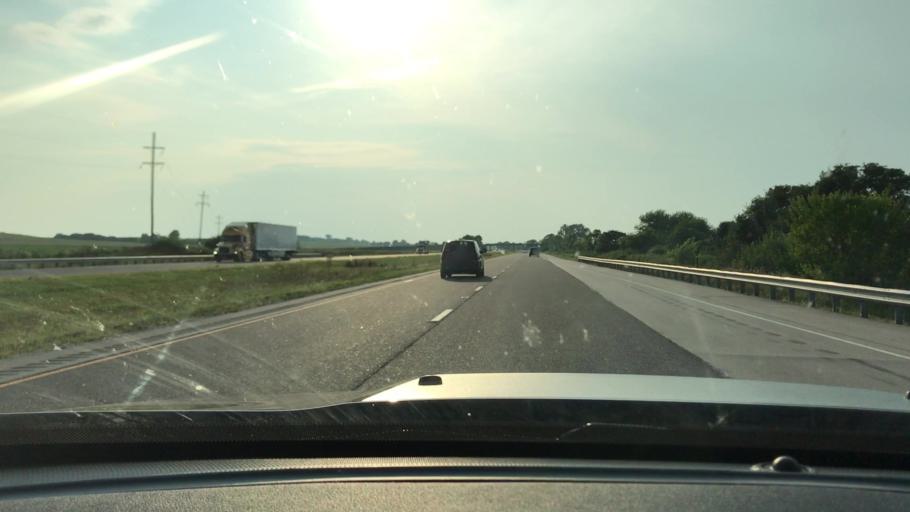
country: US
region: Illinois
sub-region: Henry County
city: Geneseo
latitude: 41.4101
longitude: -90.0209
